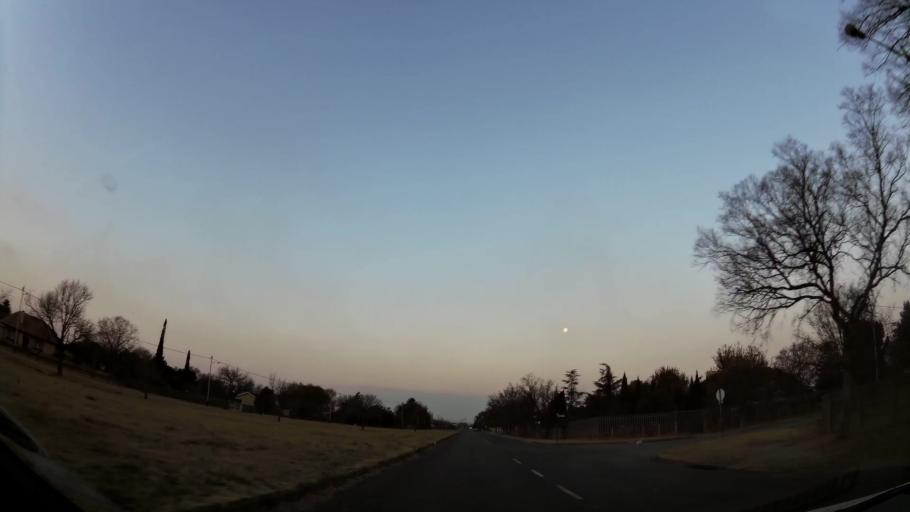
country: ZA
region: Gauteng
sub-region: Ekurhuleni Metropolitan Municipality
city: Nigel
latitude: -26.3533
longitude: 28.4369
